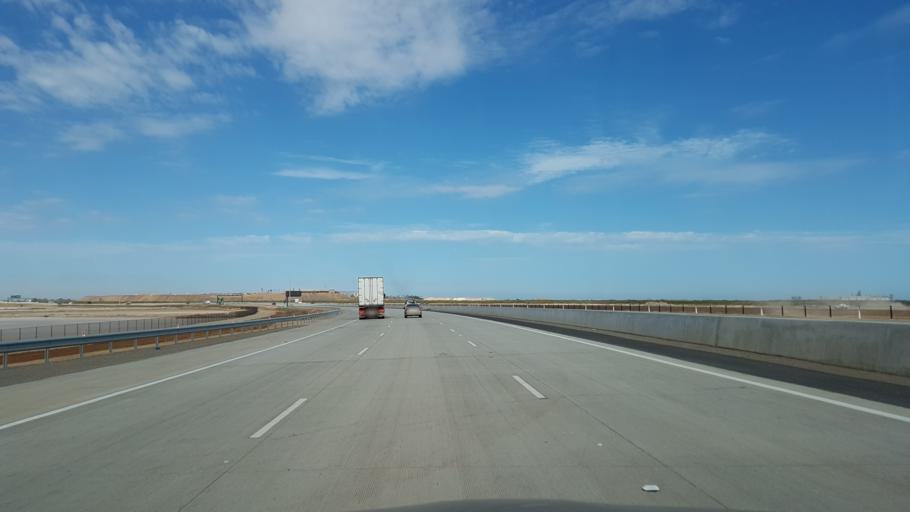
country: AU
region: South Australia
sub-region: Port Adelaide Enfield
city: Enfield
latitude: -34.8115
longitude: 138.5645
